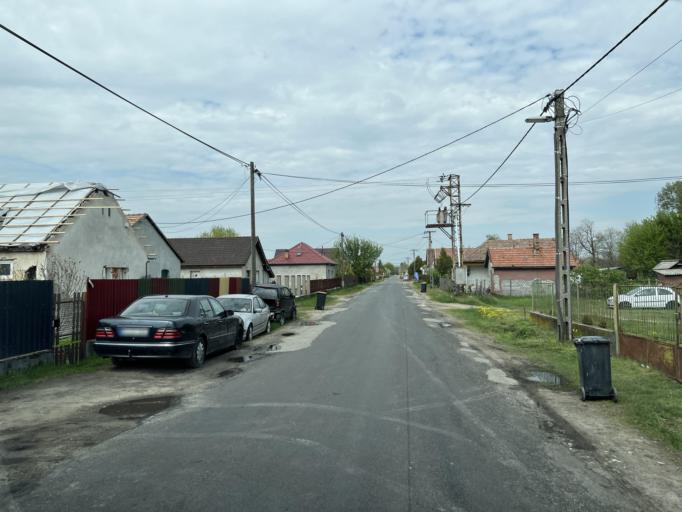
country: HU
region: Pest
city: Taborfalva
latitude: 47.1240
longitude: 19.4826
